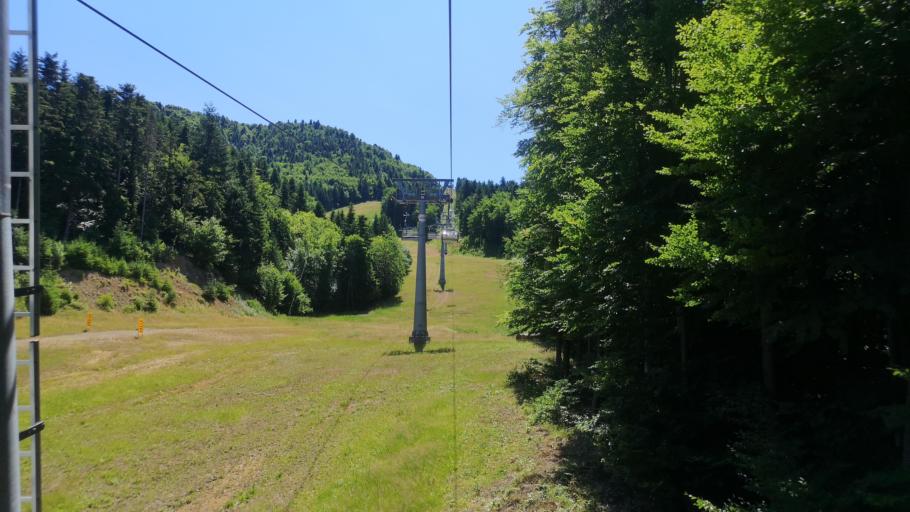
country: SK
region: Banskobystricky
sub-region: Okres Banska Bystrica
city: Banska Stiavnica
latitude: 48.4547
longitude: 18.8579
